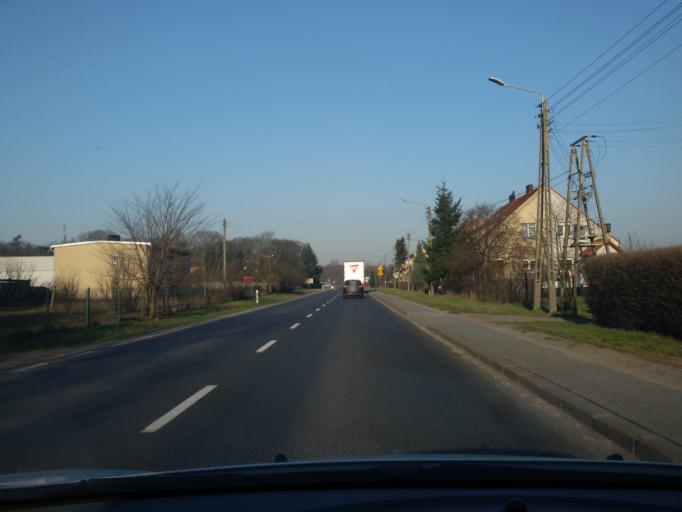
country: PL
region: Lubusz
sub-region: Powiat wschowski
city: Wschowa
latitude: 51.8192
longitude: 16.3578
